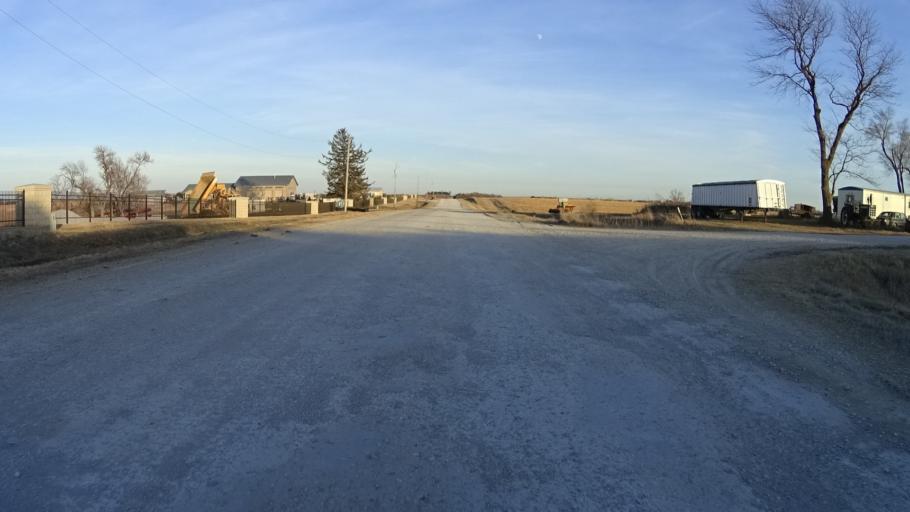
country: US
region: Nebraska
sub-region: Sarpy County
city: Springfield
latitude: 41.1325
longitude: -96.1313
